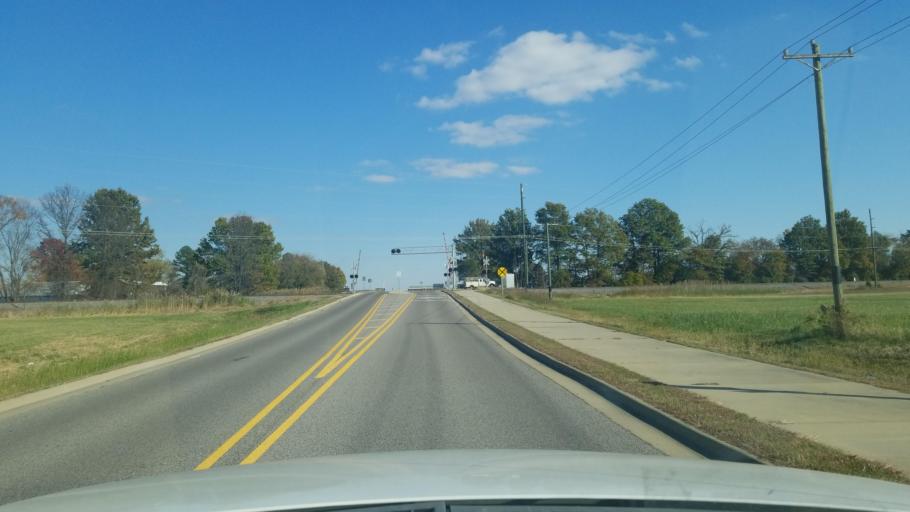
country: US
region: Illinois
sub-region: Williamson County
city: Marion
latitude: 37.7433
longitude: -88.9805
